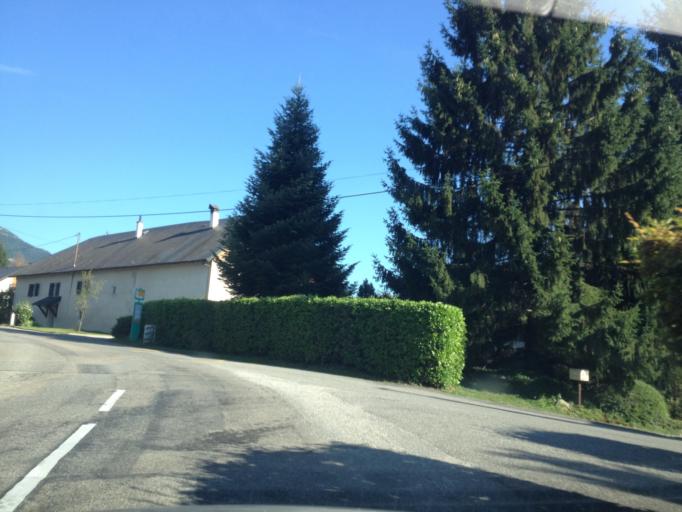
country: FR
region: Rhone-Alpes
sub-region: Departement de la Savoie
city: Sonnaz
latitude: 45.6161
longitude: 5.9060
